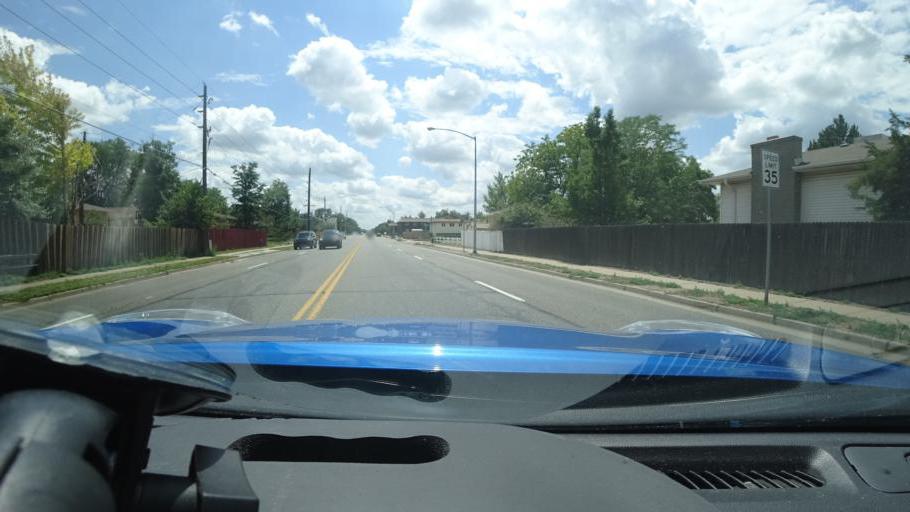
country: US
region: Colorado
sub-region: Adams County
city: Aurora
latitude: 39.7025
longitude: -104.8472
